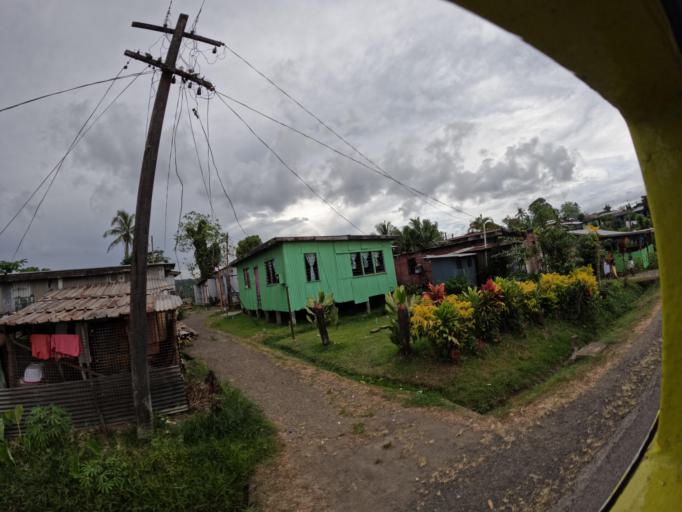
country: FJ
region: Central
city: Suva
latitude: -18.0830
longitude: 178.4547
